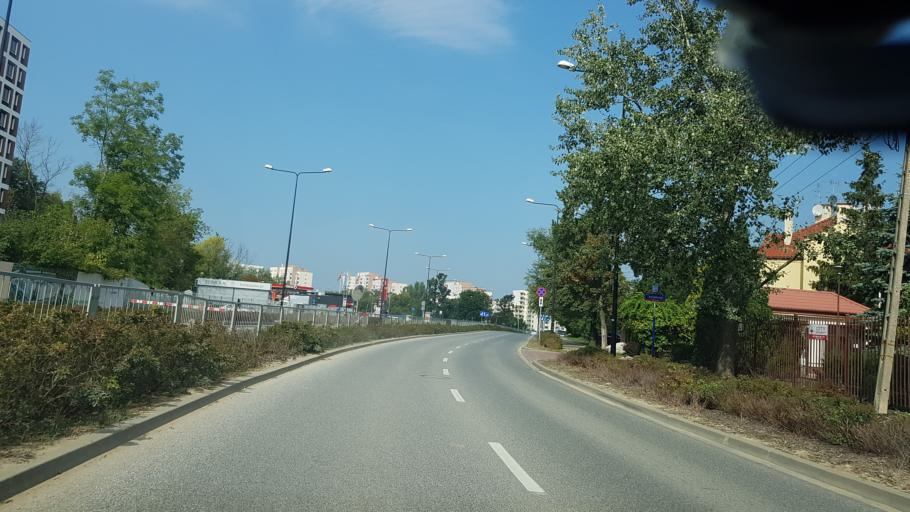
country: PL
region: Masovian Voivodeship
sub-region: Warszawa
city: Ursynow
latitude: 52.1684
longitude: 21.0427
